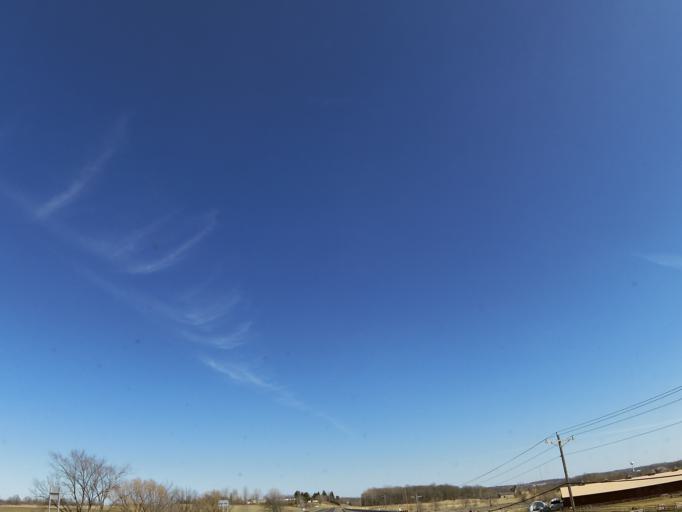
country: US
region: Minnesota
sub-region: Hennepin County
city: Medina
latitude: 45.0656
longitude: -93.6192
